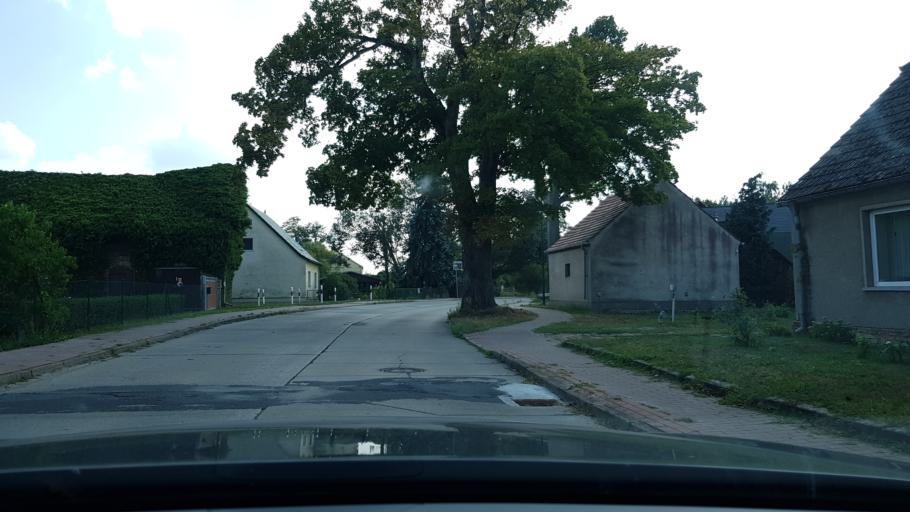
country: DE
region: Brandenburg
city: Lindow
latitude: 52.9909
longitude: 12.9725
